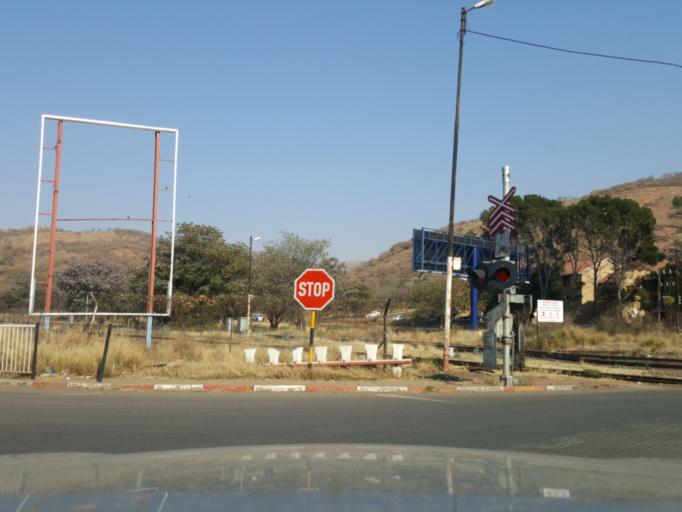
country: BW
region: South East
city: Lobatse
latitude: -25.2297
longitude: 25.6685
